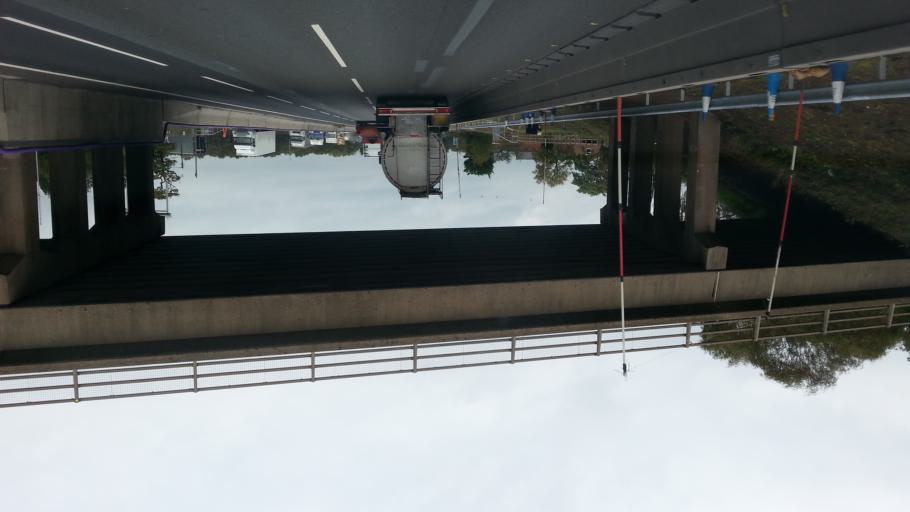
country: GB
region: England
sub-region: Cheshire East
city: Holmes Chapel
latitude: 53.2170
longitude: -2.3897
